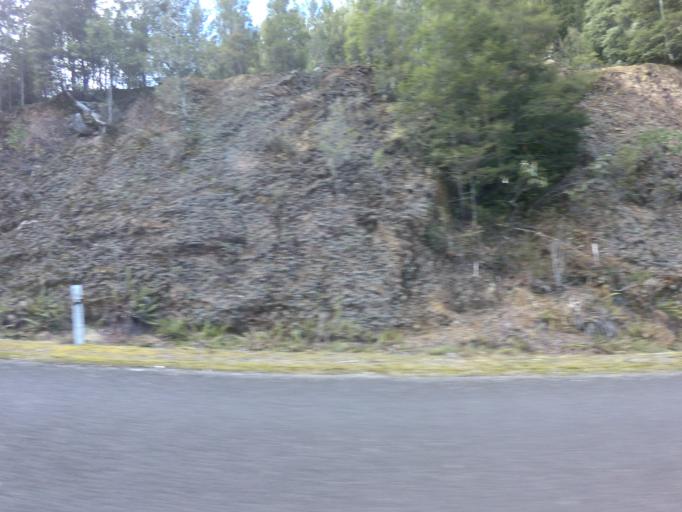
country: AU
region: Tasmania
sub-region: Huon Valley
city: Geeveston
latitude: -42.8179
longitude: 146.3448
